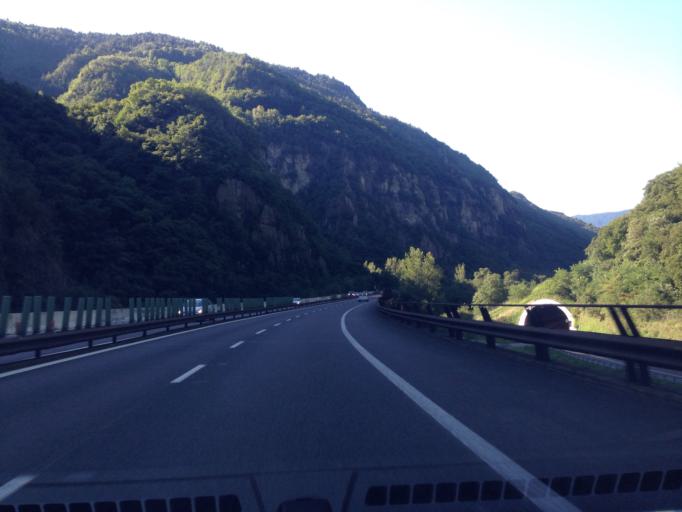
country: IT
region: Trentino-Alto Adige
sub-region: Bolzano
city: Fie Allo Sciliar
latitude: 46.5520
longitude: 11.5138
